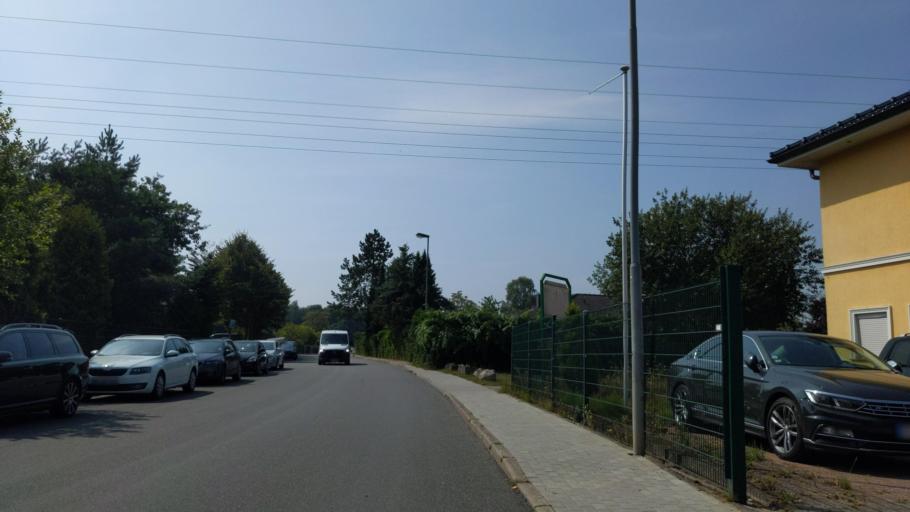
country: DE
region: Schleswig-Holstein
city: Stockelsdorf
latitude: 53.9065
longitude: 10.6484
